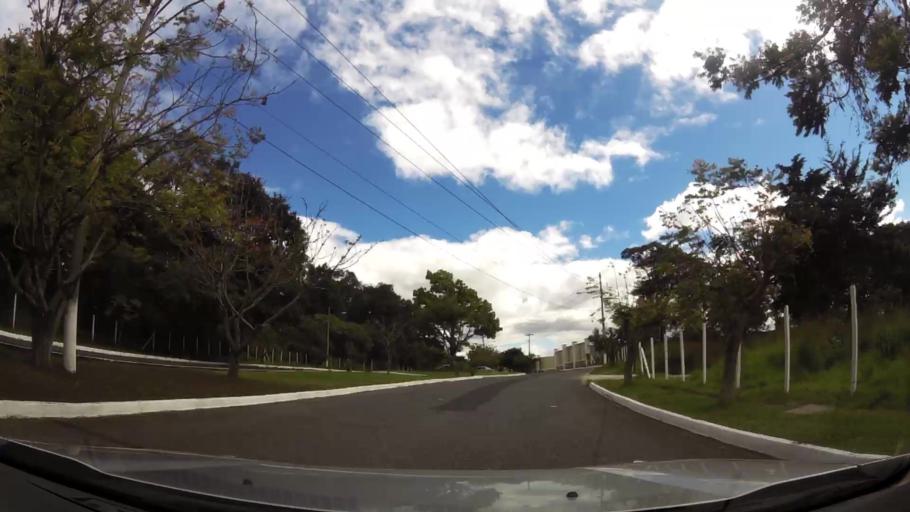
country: GT
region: Guatemala
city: Guatemala City
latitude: 14.6495
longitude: -90.5501
